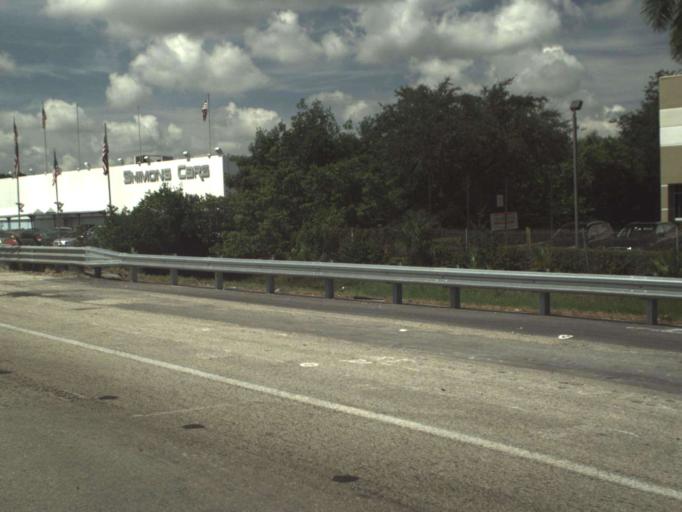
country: US
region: Florida
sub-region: Broward County
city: Dania Beach
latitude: 26.0411
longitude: -80.1635
